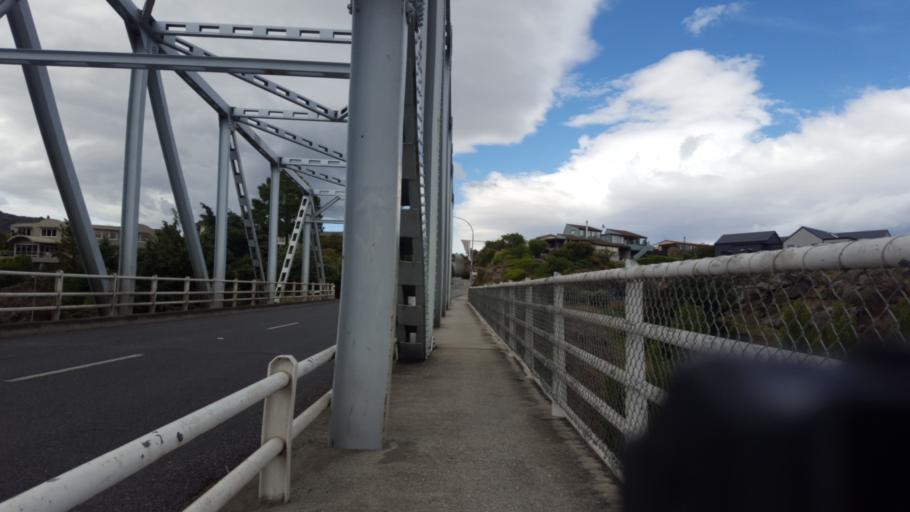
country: NZ
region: Otago
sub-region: Queenstown-Lakes District
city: Wanaka
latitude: -45.2587
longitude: 169.3903
